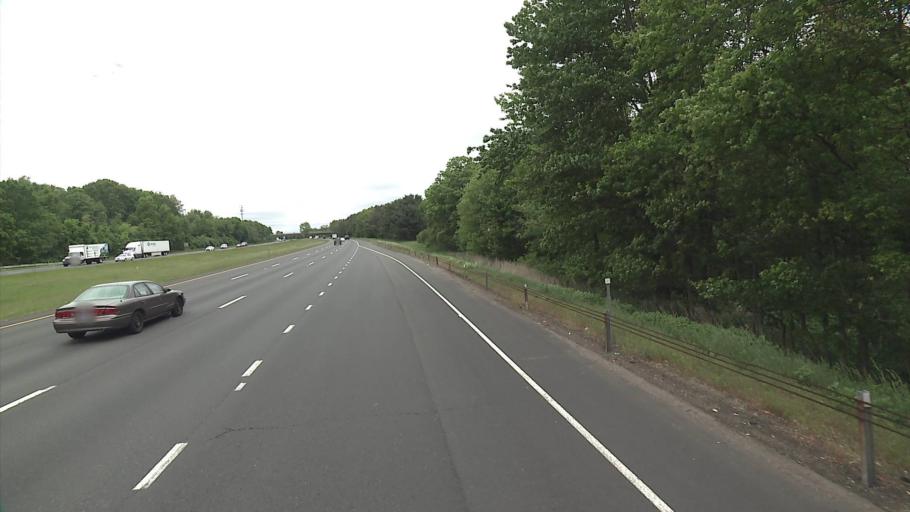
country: US
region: Connecticut
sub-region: New Haven County
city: Wallingford Center
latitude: 41.4836
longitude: -72.7682
